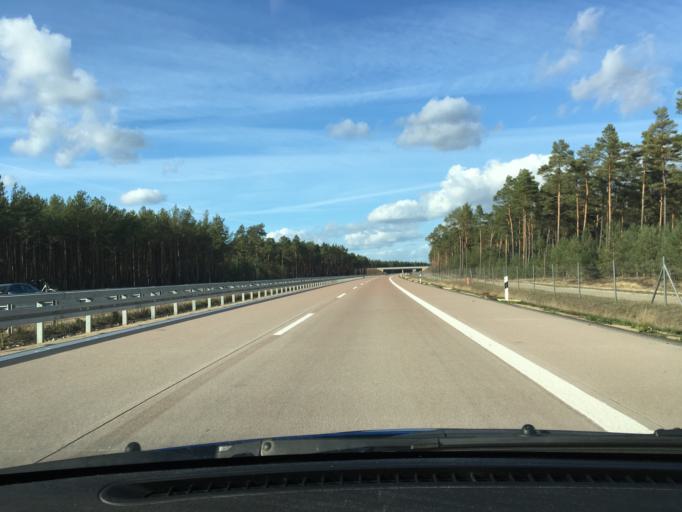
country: DE
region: Mecklenburg-Vorpommern
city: Grabow
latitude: 53.2719
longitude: 11.5289
